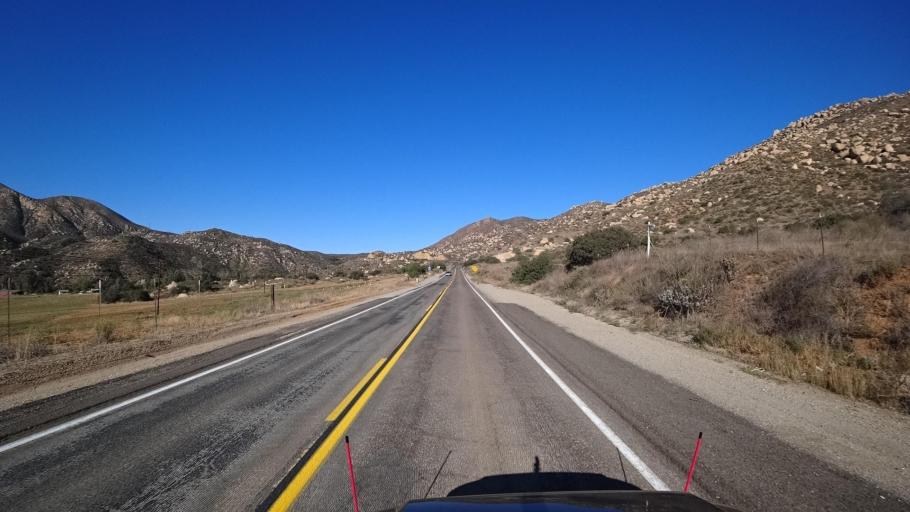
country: MX
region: Baja California
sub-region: Tecate
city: Lomas de Santa Anita
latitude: 32.6137
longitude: -116.7131
